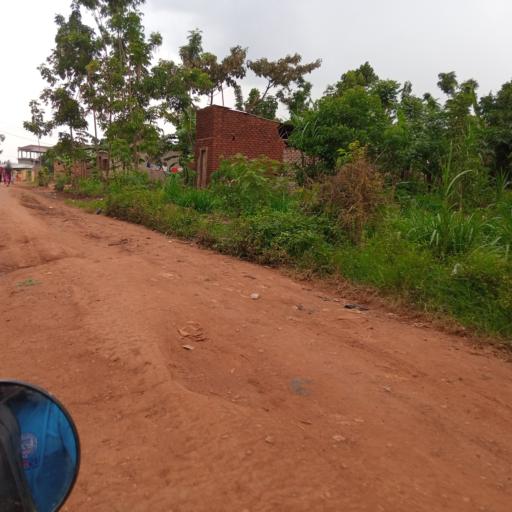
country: UG
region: Eastern Region
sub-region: Mbale District
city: Mbale
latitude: 1.1231
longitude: 34.1704
